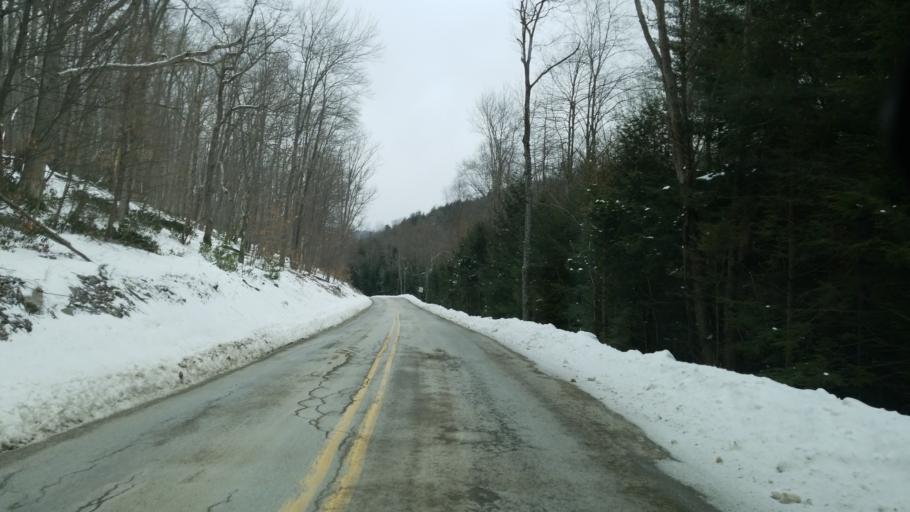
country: US
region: Pennsylvania
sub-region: Clearfield County
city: Shiloh
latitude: 41.2399
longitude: -78.1747
